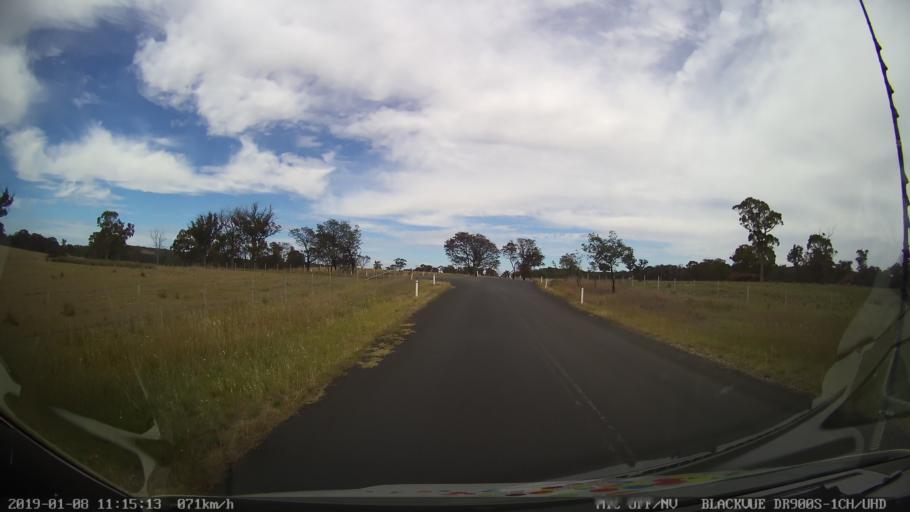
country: AU
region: New South Wales
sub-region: Guyra
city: Guyra
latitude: -30.2238
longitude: 151.5798
